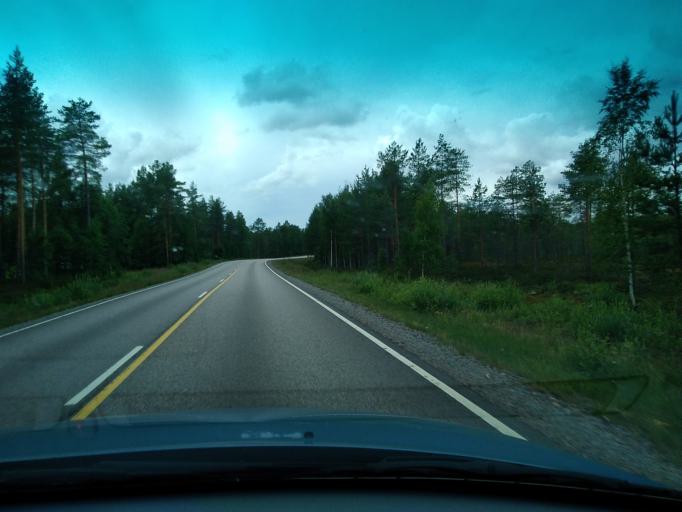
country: FI
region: Central Finland
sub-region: Saarijaervi-Viitasaari
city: Pylkoenmaeki
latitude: 62.6228
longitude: 24.7788
